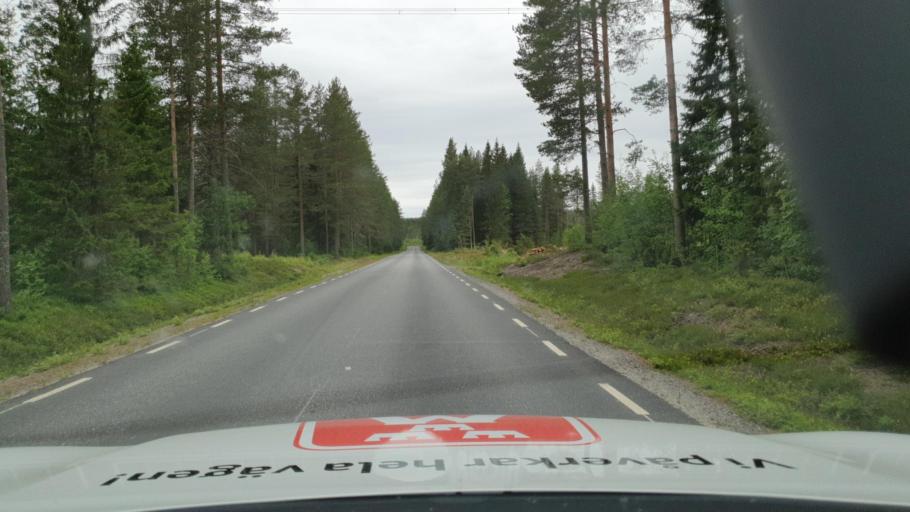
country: SE
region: Vaesterbotten
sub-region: Nordmalings Kommun
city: Nordmaling
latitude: 63.7176
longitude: 19.5686
